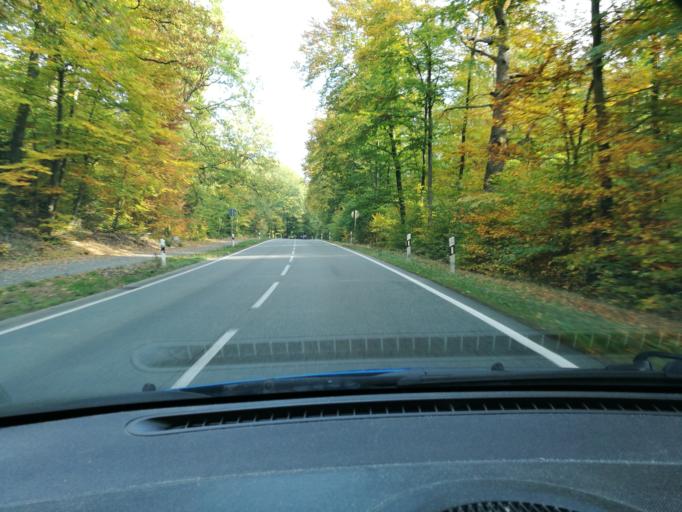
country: DE
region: Lower Saxony
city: Gohrde
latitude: 53.1357
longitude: 10.8860
